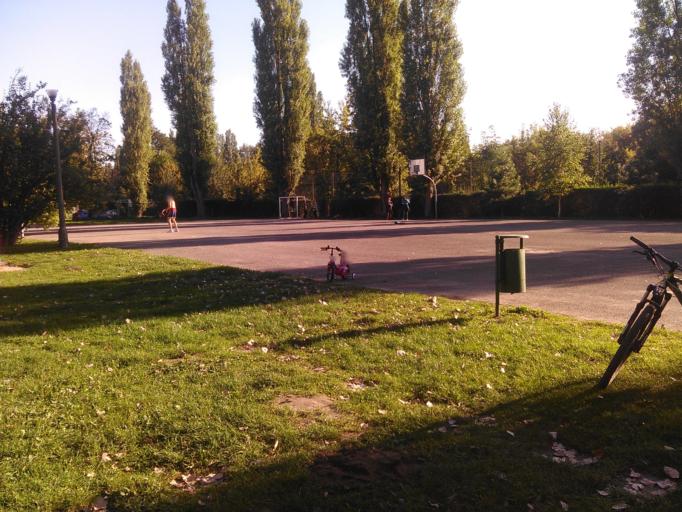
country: PL
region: Lesser Poland Voivodeship
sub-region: Krakow
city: Krakow
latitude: 50.0718
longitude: 19.9684
